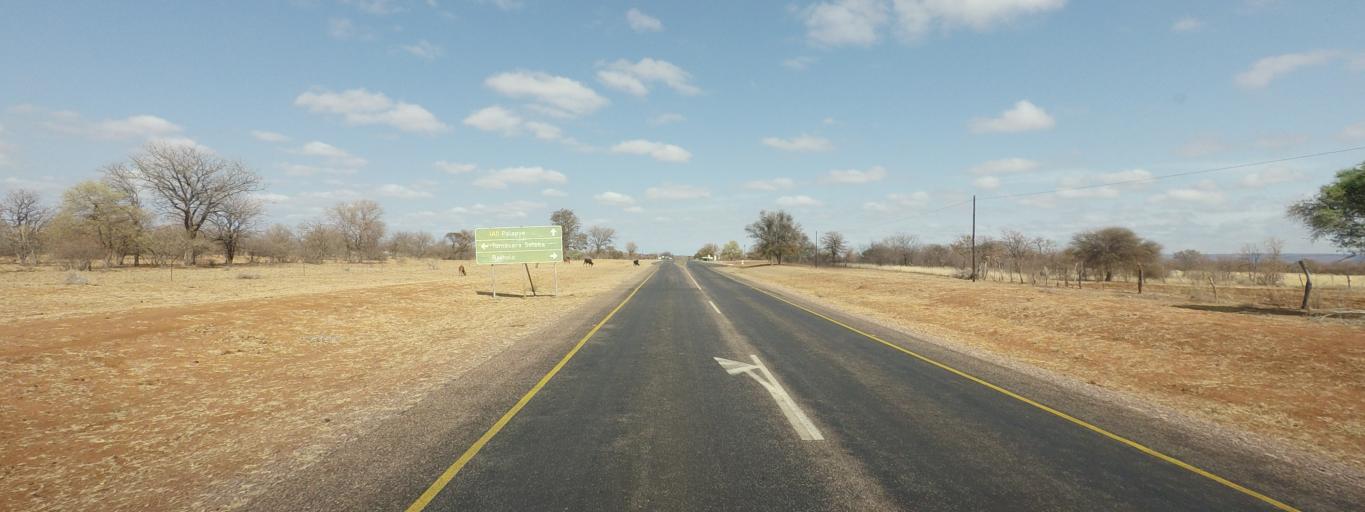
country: BW
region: Central
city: Ramokgonami
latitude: -22.8018
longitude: 27.4961
